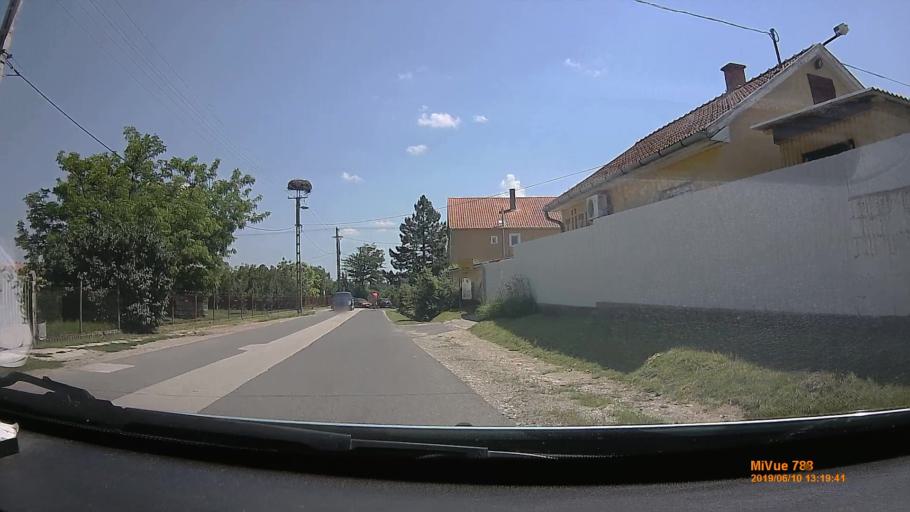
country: HU
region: Borsod-Abauj-Zemplen
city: Tiszaluc
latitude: 48.0405
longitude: 21.0763
